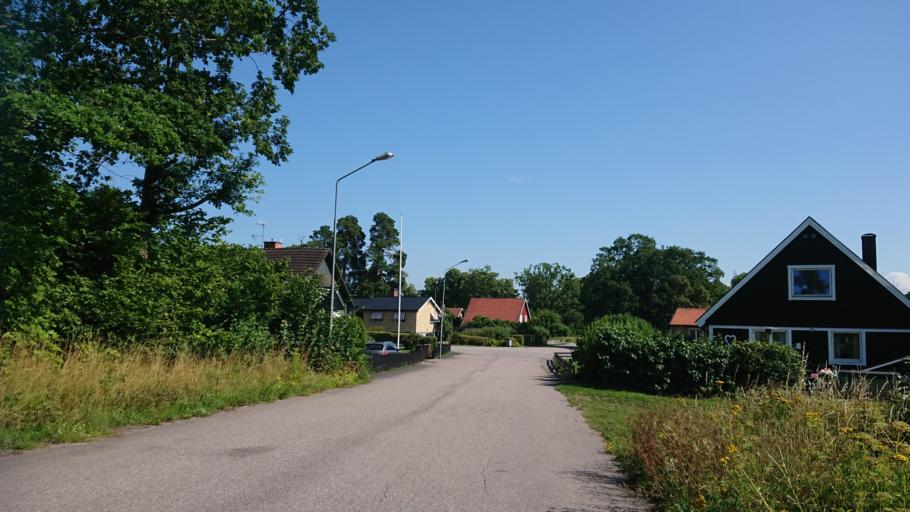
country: SE
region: Uppsala
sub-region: Osthammars Kommun
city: Osterbybruk
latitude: 60.1979
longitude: 17.9072
